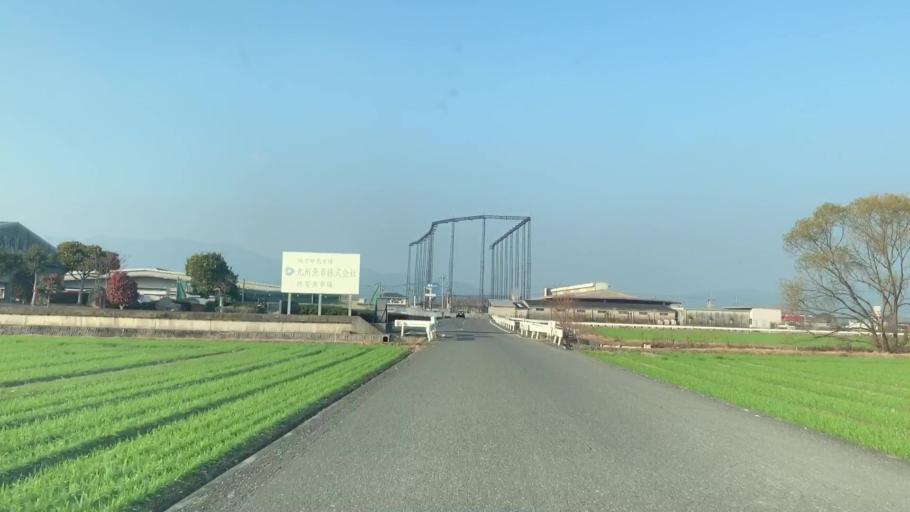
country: JP
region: Saga Prefecture
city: Saga-shi
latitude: 33.2625
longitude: 130.2481
